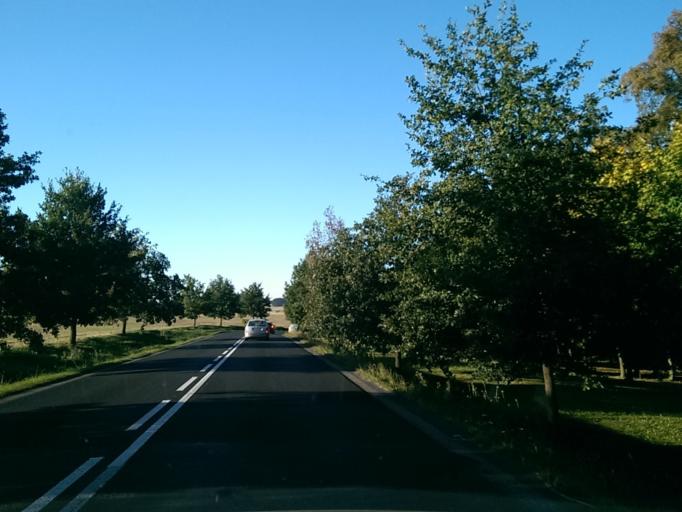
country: CZ
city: Duba
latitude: 50.5466
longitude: 14.5433
